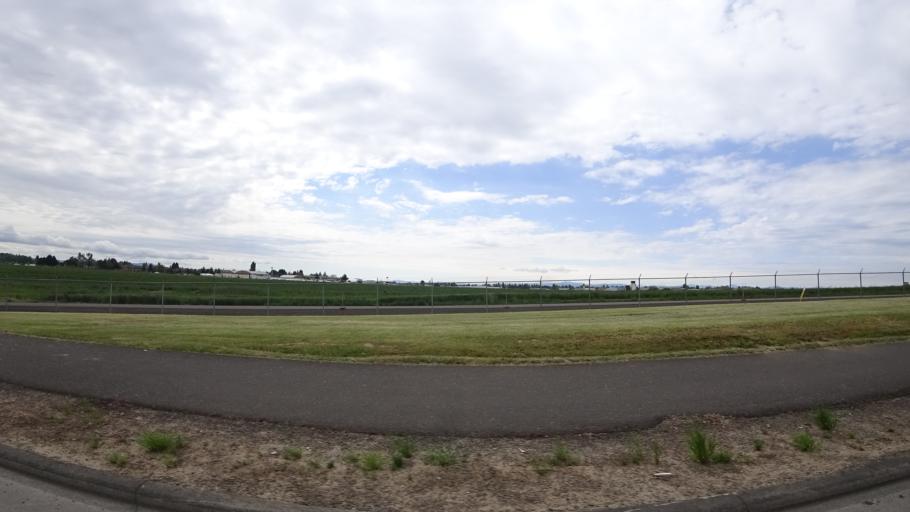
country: US
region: Oregon
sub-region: Washington County
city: Hillsboro
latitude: 45.5362
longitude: -122.9416
